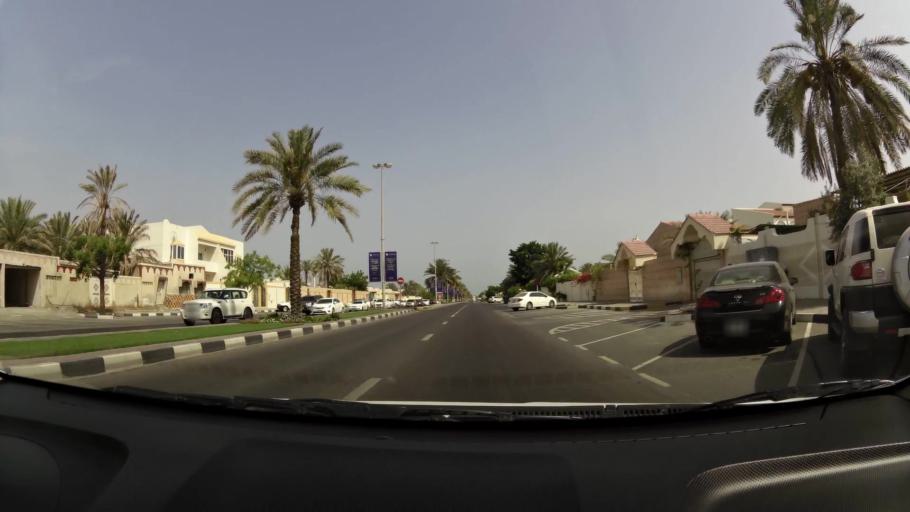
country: AE
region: Ash Shariqah
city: Sharjah
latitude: 25.3579
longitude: 55.4260
